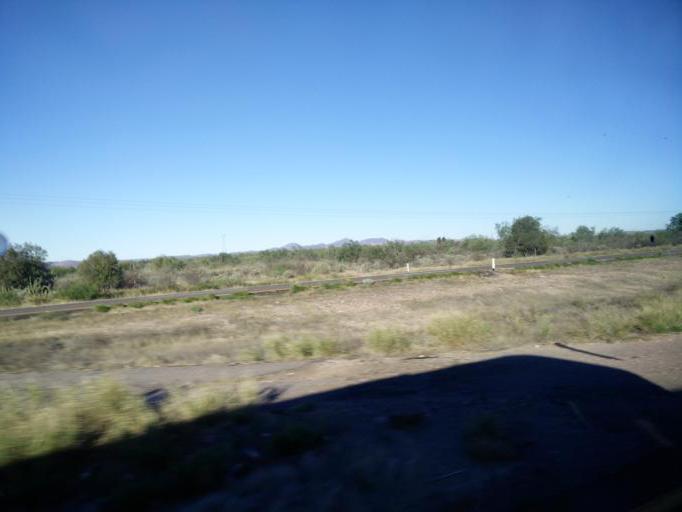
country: MX
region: Sonora
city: Heroica Guaymas
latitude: 28.1415
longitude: -110.9740
